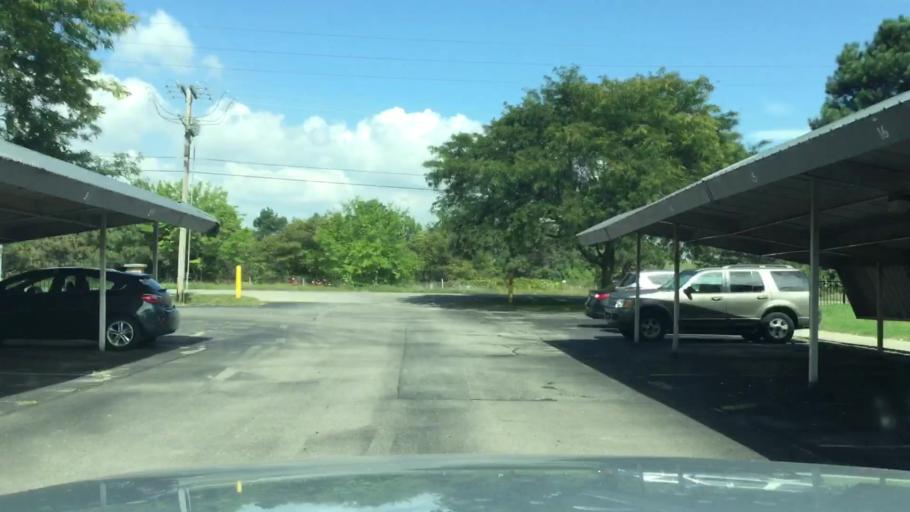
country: US
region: Michigan
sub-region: Wayne County
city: Belleville
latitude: 42.2181
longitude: -83.5140
